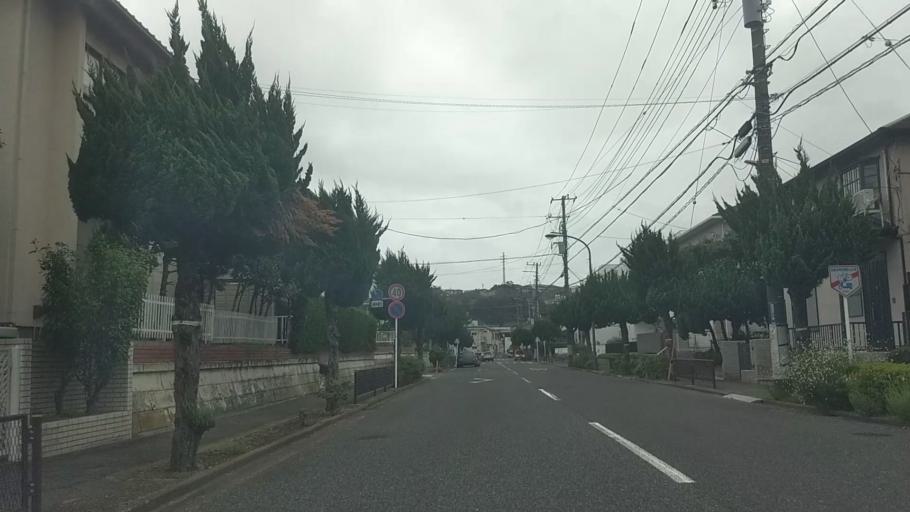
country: JP
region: Kanagawa
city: Yokosuka
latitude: 35.2617
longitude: 139.7058
